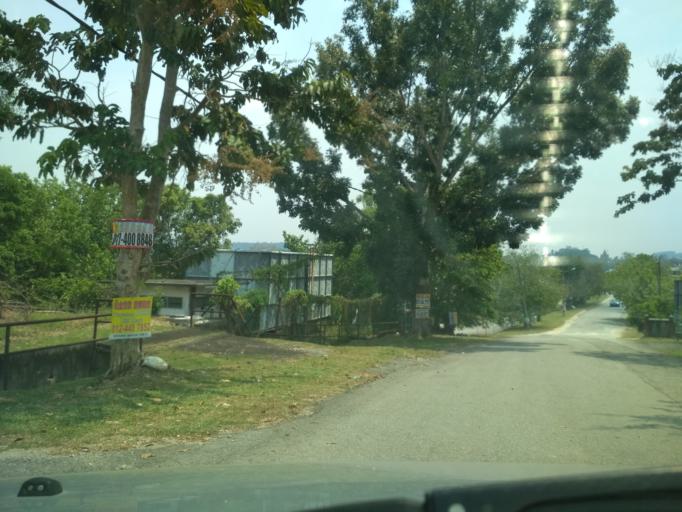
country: MY
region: Kedah
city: Kulim
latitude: 5.3549
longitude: 100.5333
